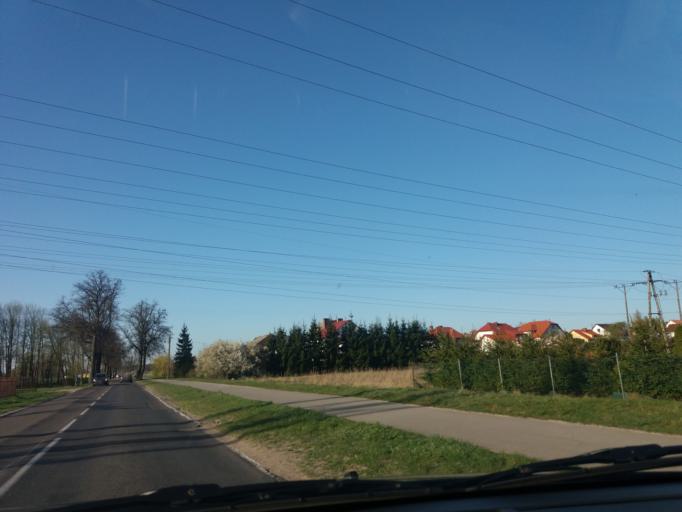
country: PL
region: Warmian-Masurian Voivodeship
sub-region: Powiat nidzicki
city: Nidzica
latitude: 53.3754
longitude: 20.4301
